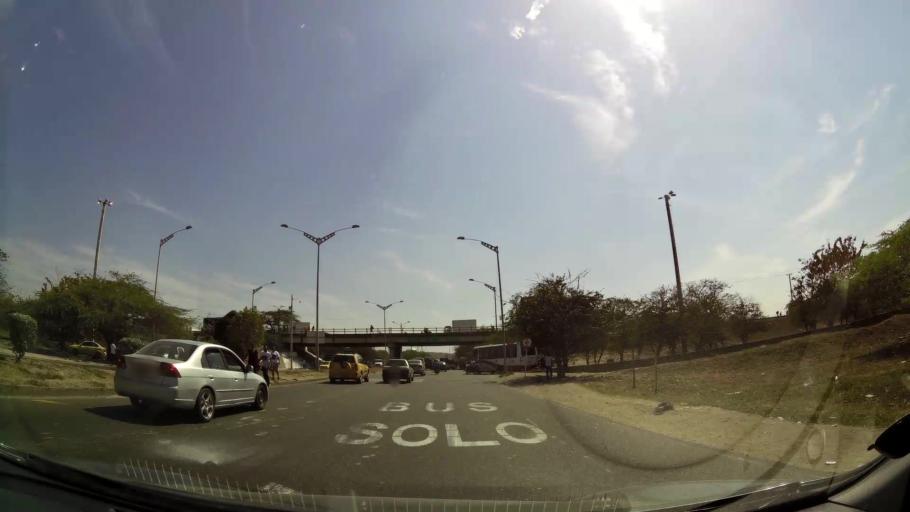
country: CO
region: Atlantico
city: Barranquilla
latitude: 10.9440
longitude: -74.8337
